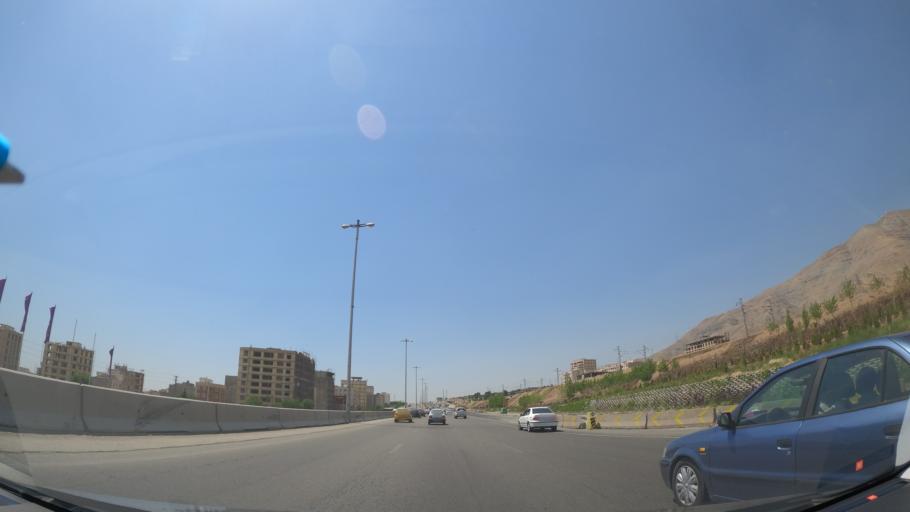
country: IR
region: Tehran
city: Shahr-e Qods
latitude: 35.7547
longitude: 51.0742
